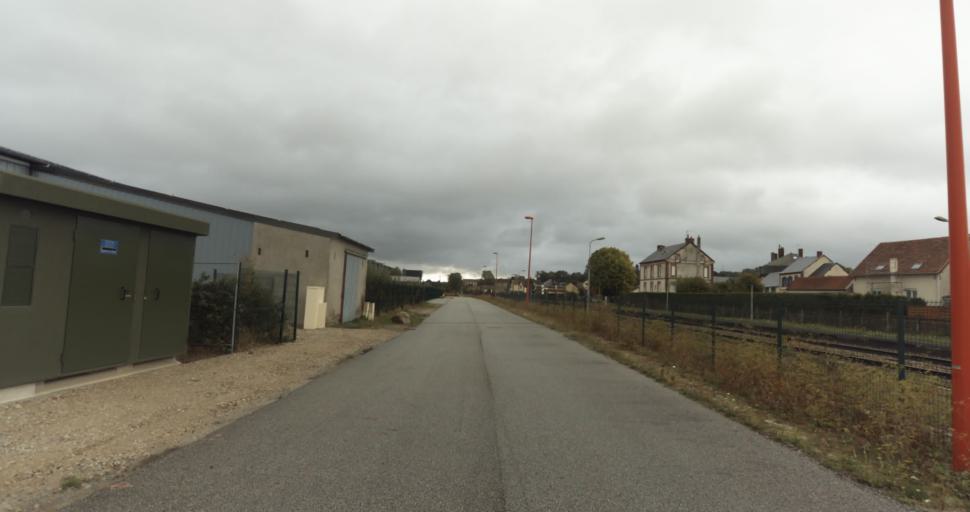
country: FR
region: Lower Normandy
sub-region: Departement de l'Orne
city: Sainte-Gauburge-Sainte-Colombe
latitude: 48.7174
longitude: 0.4273
